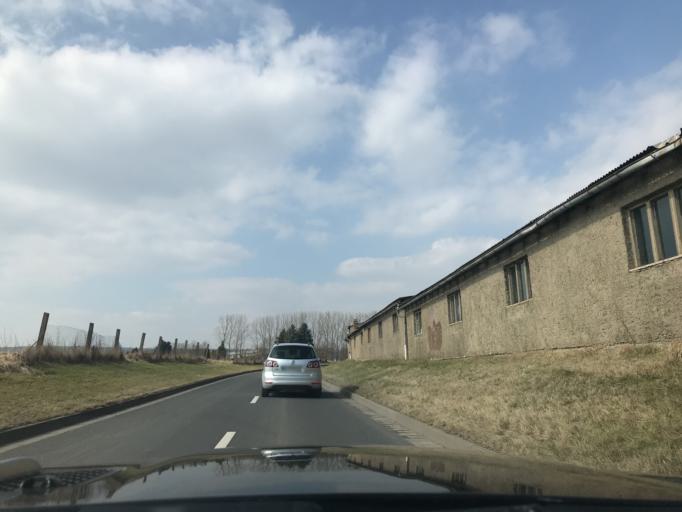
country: DE
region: Thuringia
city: Oberdorla
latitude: 51.1682
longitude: 10.4174
